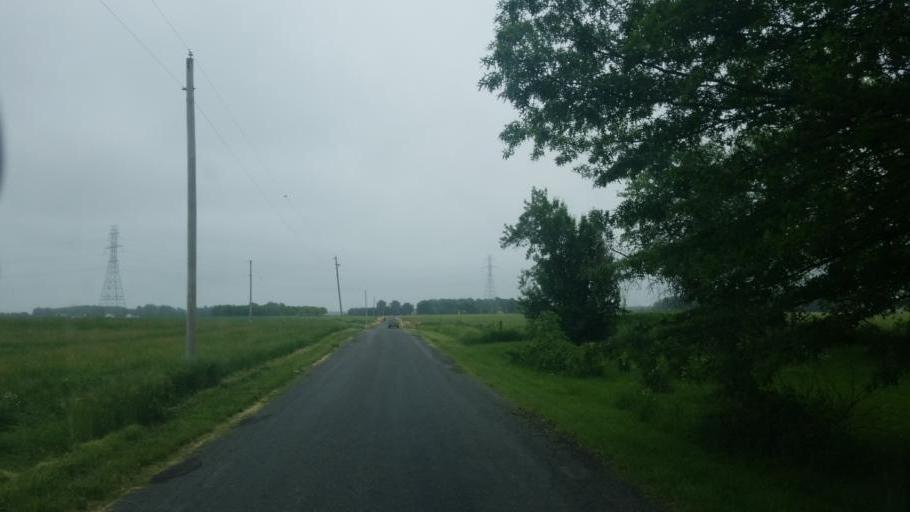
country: US
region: Indiana
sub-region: Marshall County
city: Bremen
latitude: 41.4793
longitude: -86.1339
